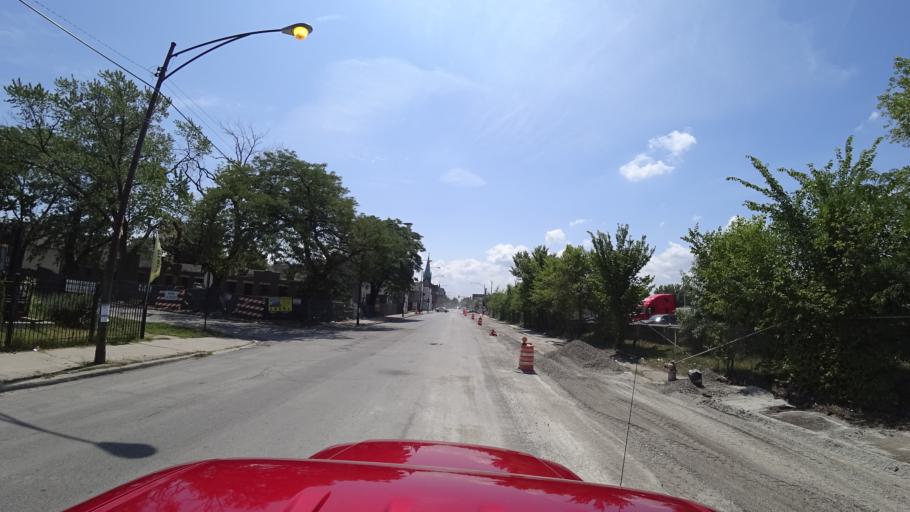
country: US
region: Illinois
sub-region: Cook County
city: Chicago
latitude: 41.8258
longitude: -87.6947
